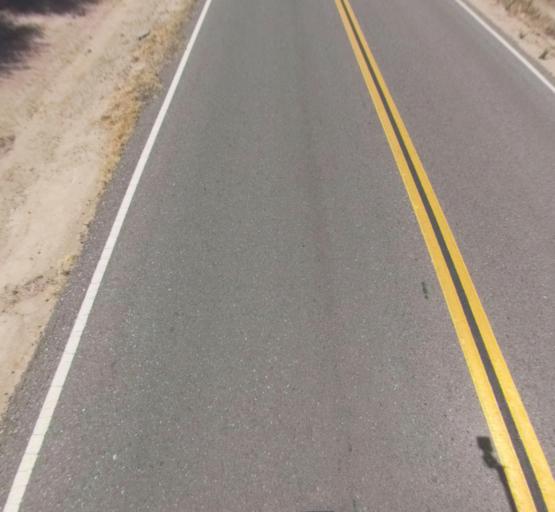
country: US
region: California
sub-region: Madera County
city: Chowchilla
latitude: 37.0552
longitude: -120.3830
